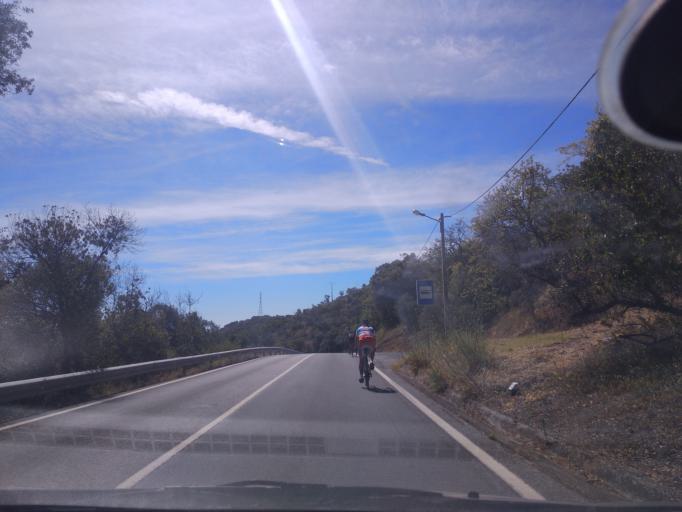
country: PT
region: Faro
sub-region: Sao Bras de Alportel
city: Sao Bras de Alportel
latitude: 37.1549
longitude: -7.8353
